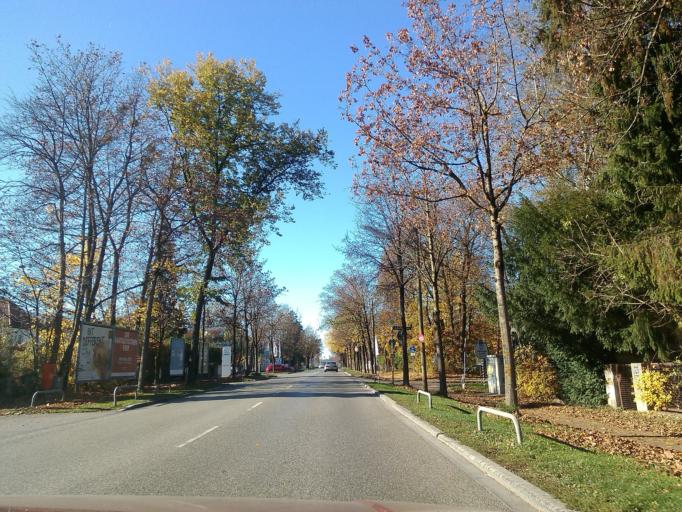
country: DE
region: Bavaria
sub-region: Upper Bavaria
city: Grafelfing
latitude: 48.1422
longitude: 11.4186
